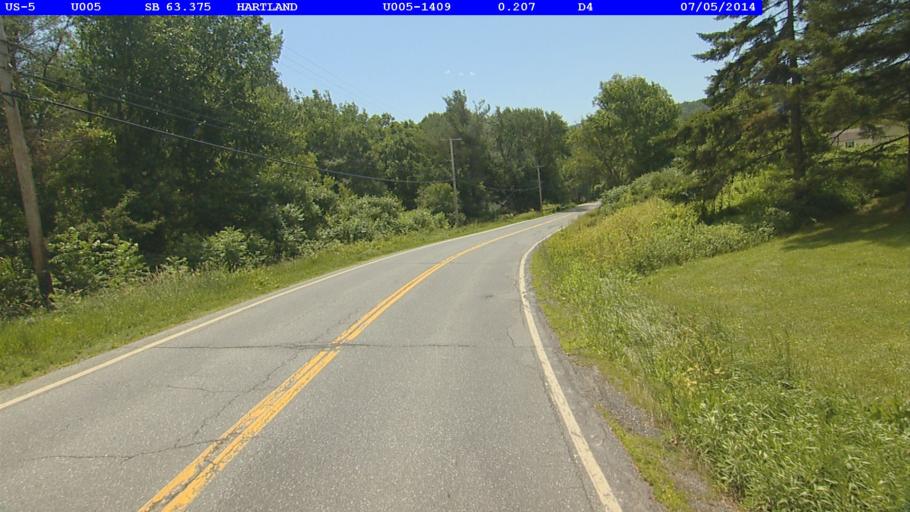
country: US
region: Vermont
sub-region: Windsor County
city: Windsor
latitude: 43.5229
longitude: -72.3994
